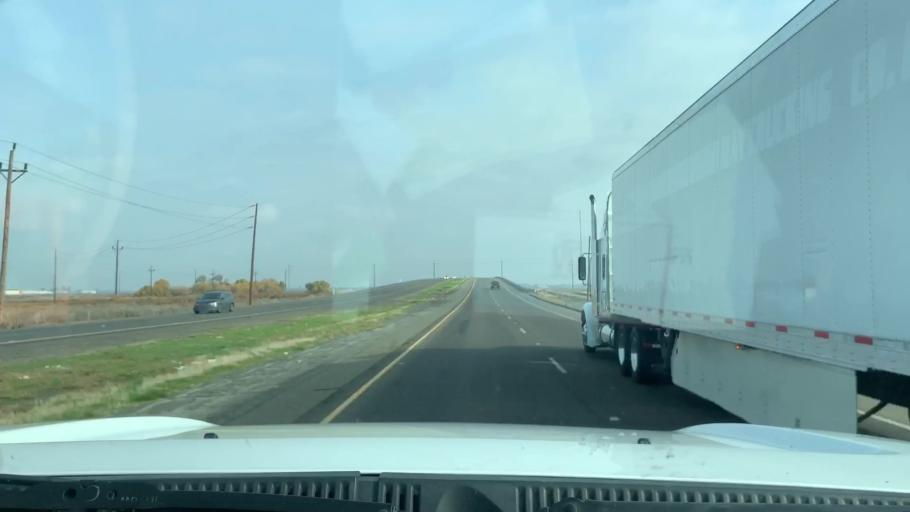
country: US
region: California
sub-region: Kings County
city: Lemoore Station
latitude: 36.2683
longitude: -119.8398
